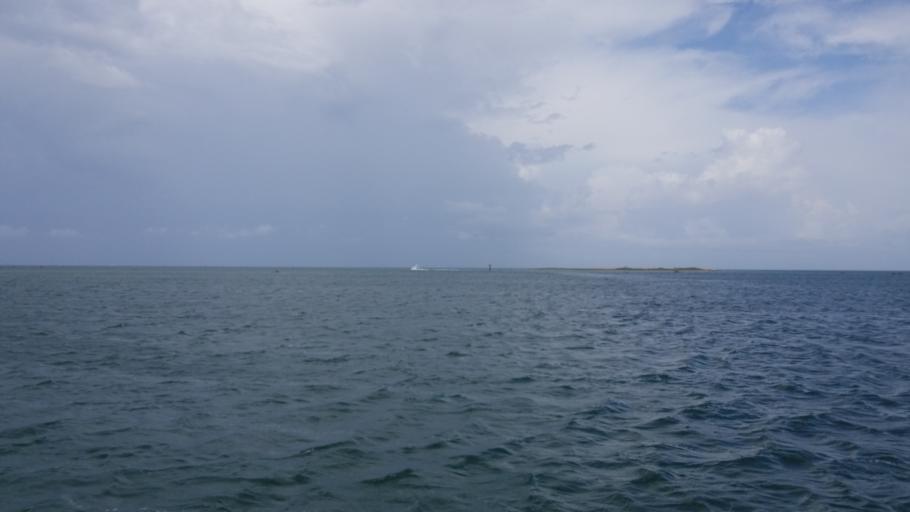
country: US
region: North Carolina
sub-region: Dare County
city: Buxton
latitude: 35.2107
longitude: -75.7072
